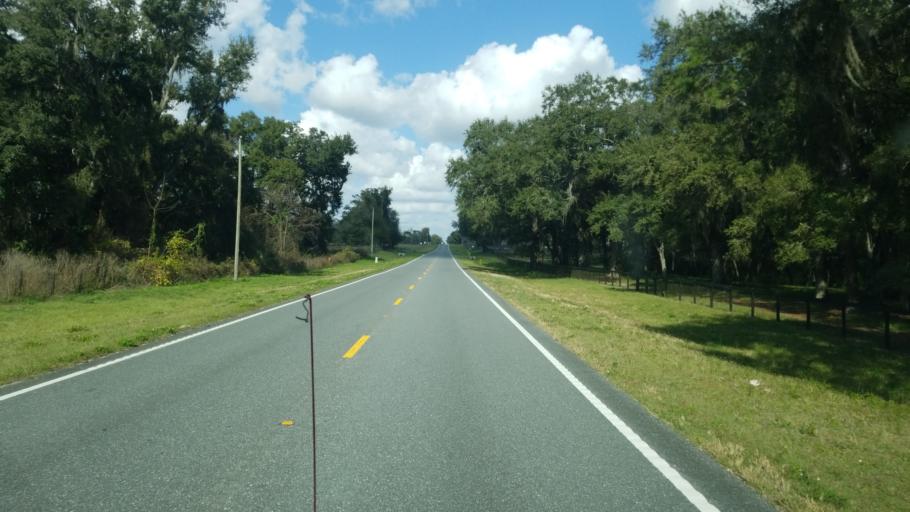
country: US
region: Florida
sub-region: Sumter County
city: Wildwood
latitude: 28.9000
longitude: -82.1200
